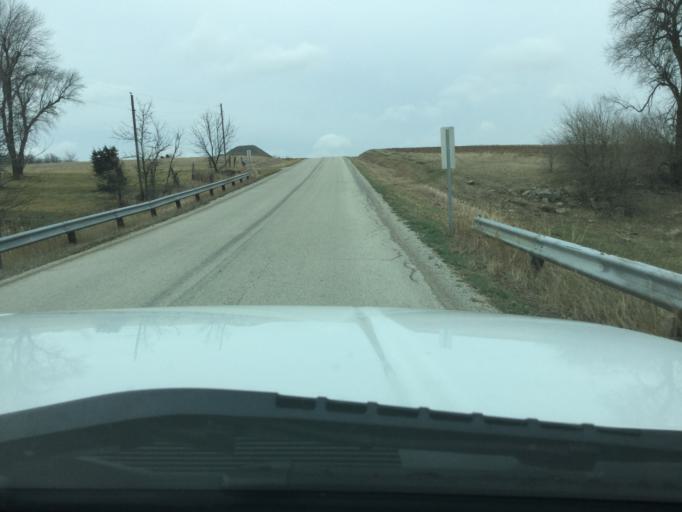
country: US
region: Kansas
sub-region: Nemaha County
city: Sabetha
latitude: 39.8538
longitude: -95.7142
